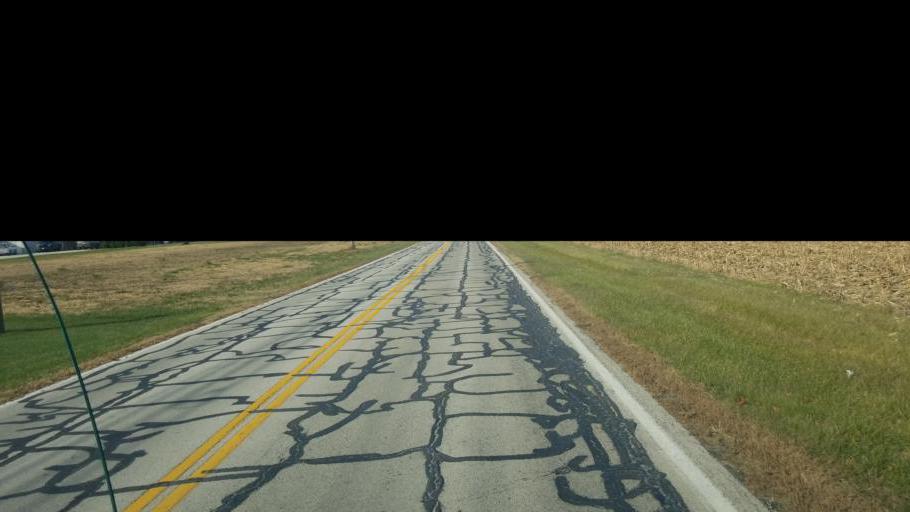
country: US
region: Ohio
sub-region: Mercer County
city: Celina
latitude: 40.5652
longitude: -84.5873
